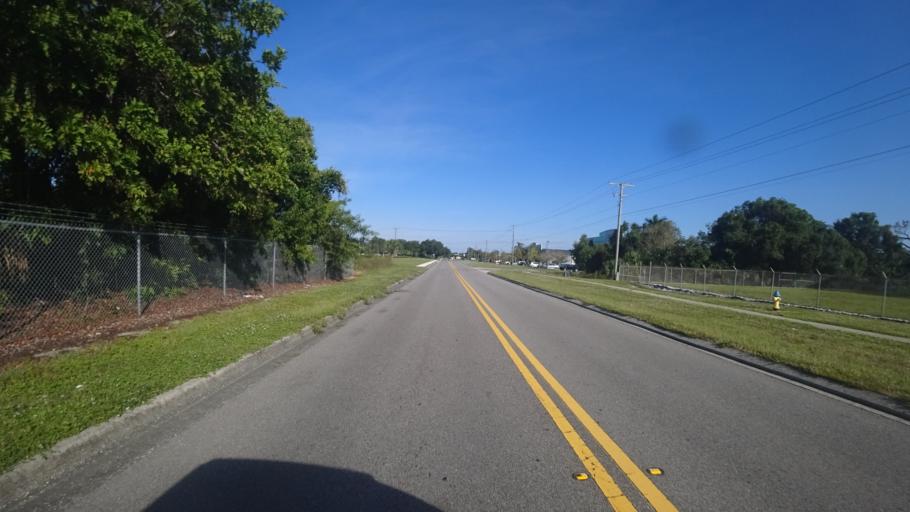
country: US
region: Florida
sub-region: Manatee County
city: Whitfield
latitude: 27.4076
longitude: -82.5636
